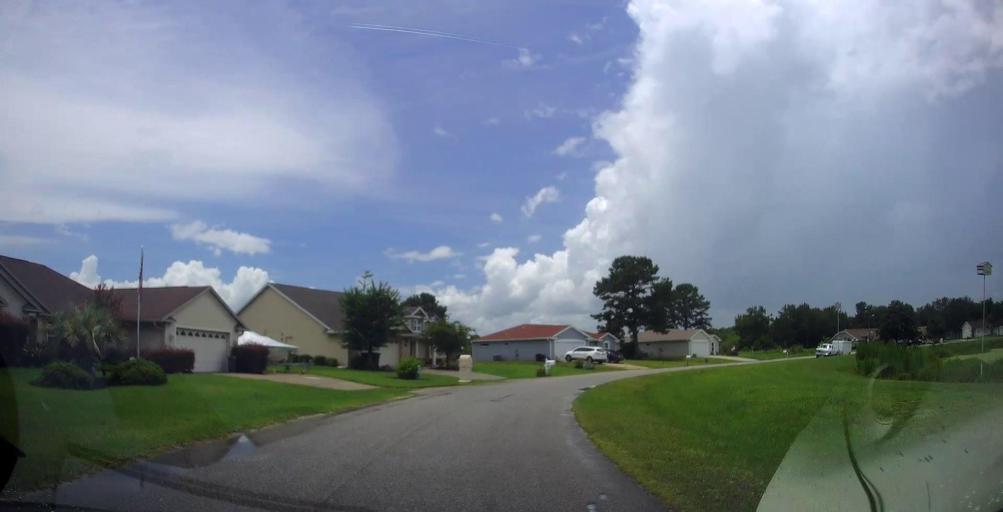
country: US
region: Florida
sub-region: Marion County
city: Silver Springs Shores
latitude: 29.1325
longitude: -82.0117
